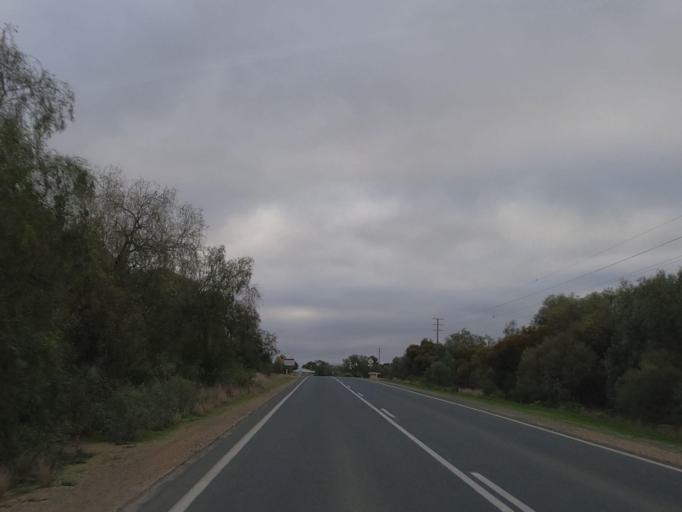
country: AU
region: Victoria
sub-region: Swan Hill
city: Swan Hill
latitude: -35.4682
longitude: 143.6594
